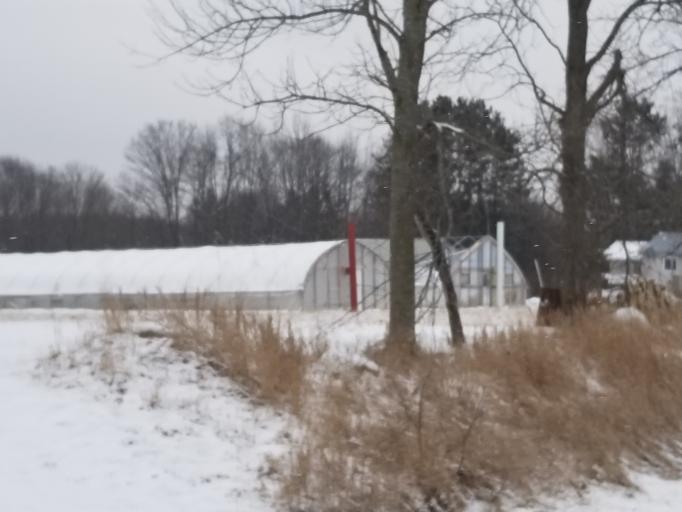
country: US
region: Michigan
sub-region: Osceola County
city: Evart
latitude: 44.1145
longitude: -85.2063
